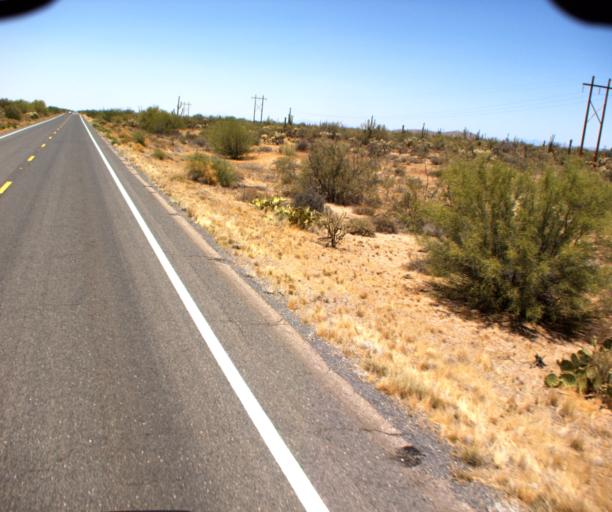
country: US
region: Arizona
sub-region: Pinal County
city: Florence
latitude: 32.8174
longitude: -111.1991
